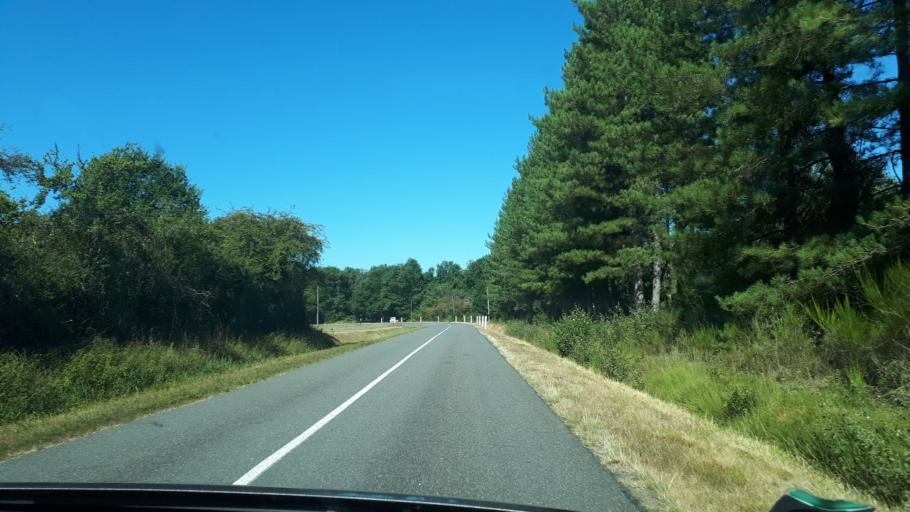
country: FR
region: Centre
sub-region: Departement du Loiret
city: Cerdon
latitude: 47.6413
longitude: 2.4028
